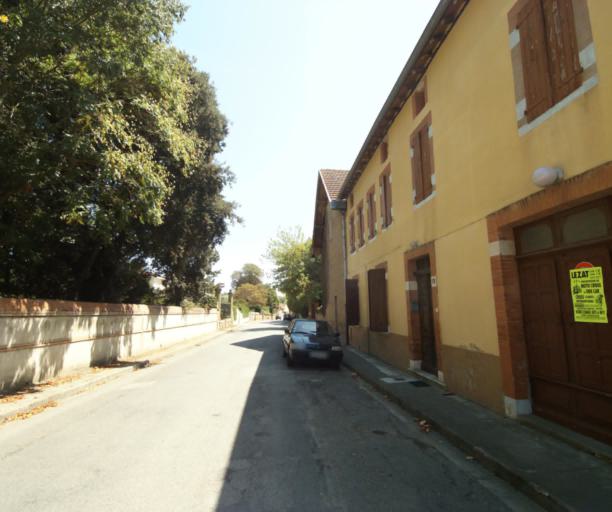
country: FR
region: Midi-Pyrenees
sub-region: Departement de l'Ariege
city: Lezat-sur-Leze
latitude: 43.2751
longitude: 1.3494
